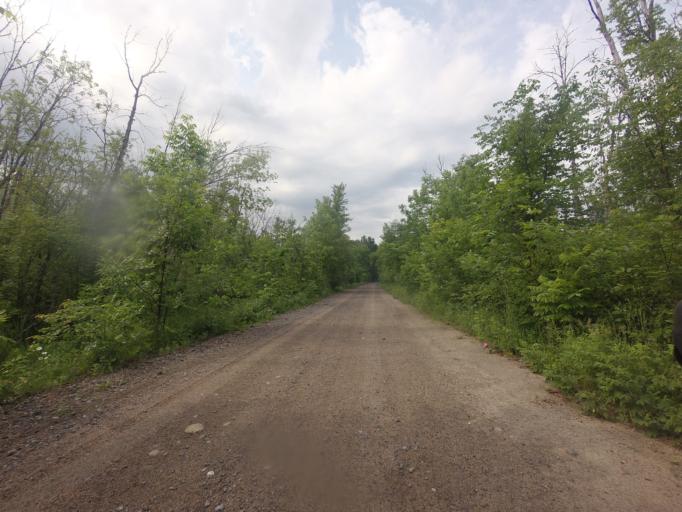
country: CA
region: Quebec
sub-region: Outaouais
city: Maniwaki
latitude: 46.3258
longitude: -76.0047
